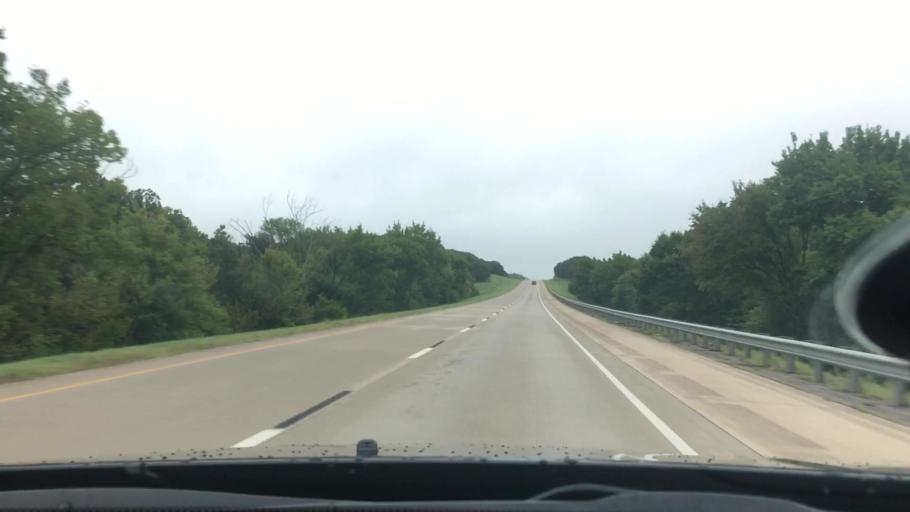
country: US
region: Oklahoma
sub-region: Okfuskee County
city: Boley
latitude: 35.3844
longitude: -96.5788
